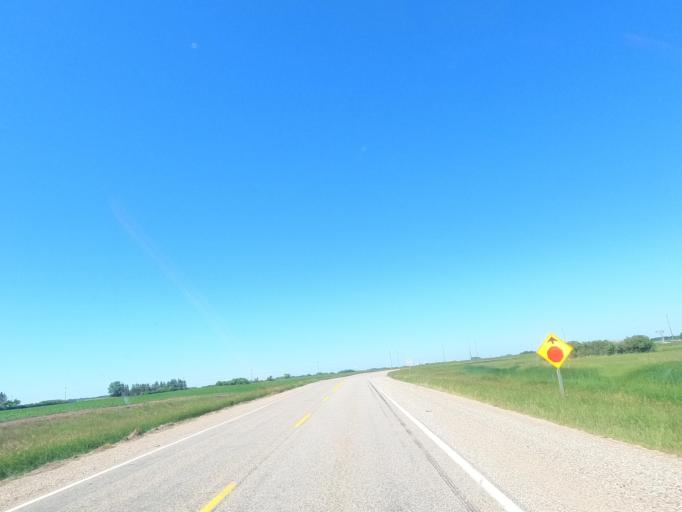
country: CA
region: Manitoba
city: Brandon
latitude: 49.5871
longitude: -99.9574
